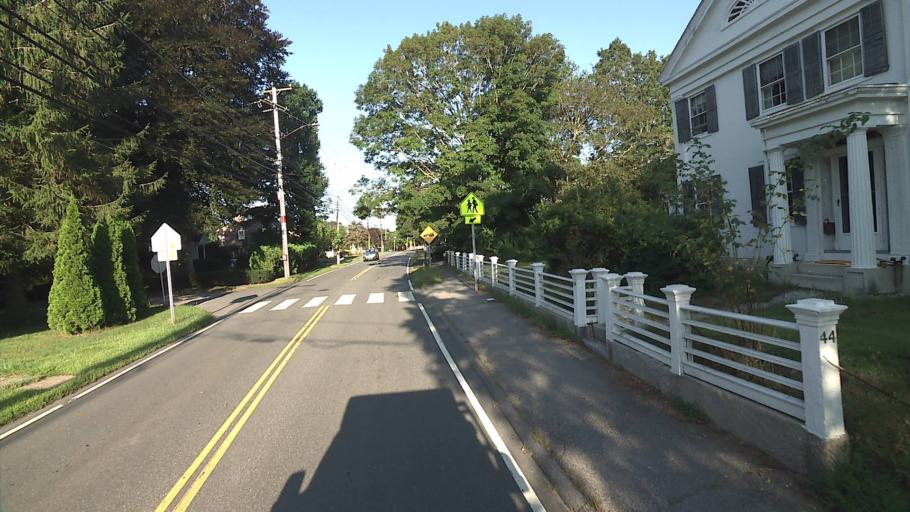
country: US
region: Connecticut
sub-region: New London County
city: Mystic
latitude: 41.3530
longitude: -71.9804
